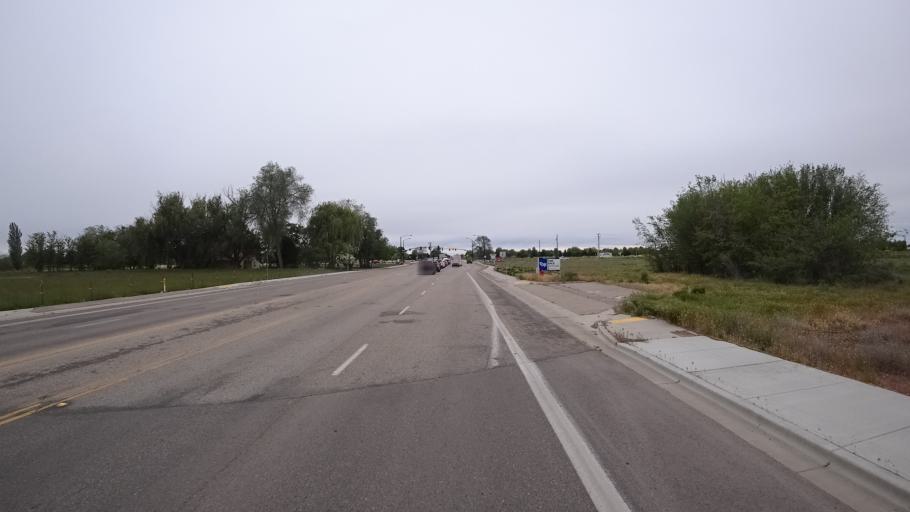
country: US
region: Idaho
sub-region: Ada County
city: Meridian
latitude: 43.6339
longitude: -116.4119
